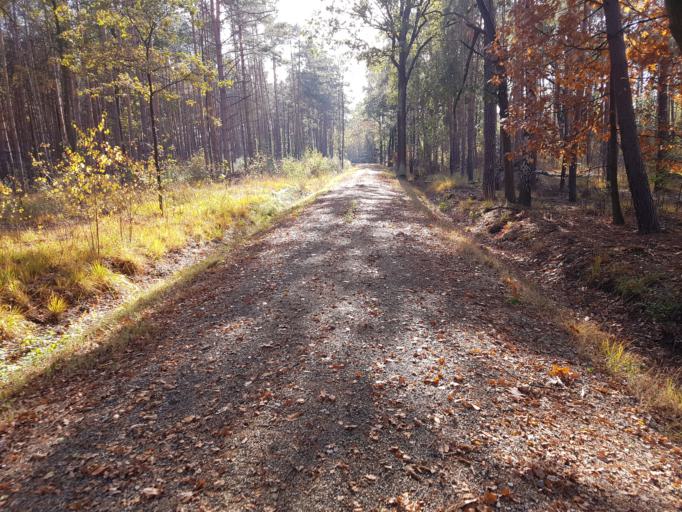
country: DE
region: Brandenburg
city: Schilda
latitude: 51.5915
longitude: 13.3422
